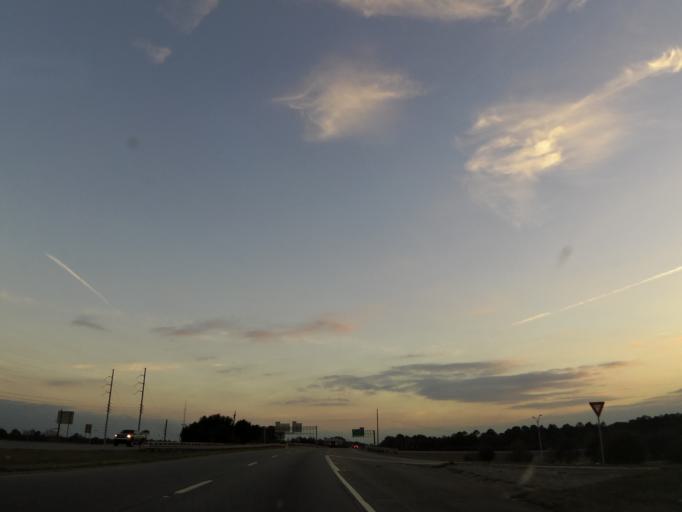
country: US
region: Georgia
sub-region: Dougherty County
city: Albany
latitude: 31.5730
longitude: -84.1114
